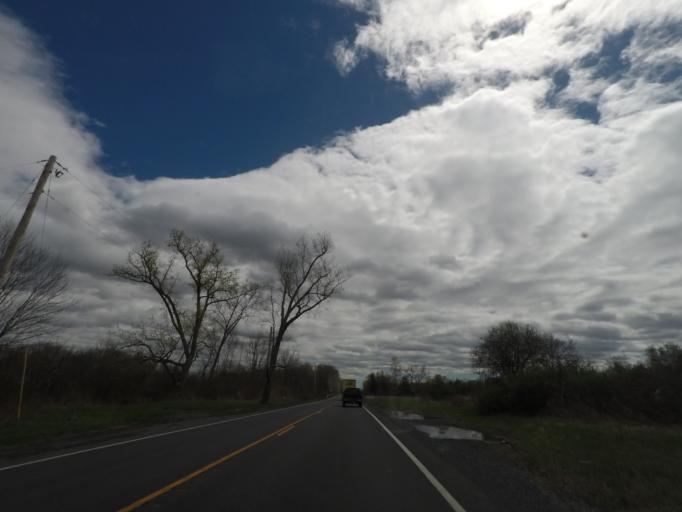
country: US
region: New York
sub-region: Albany County
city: Ravena
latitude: 42.4979
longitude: -73.7953
